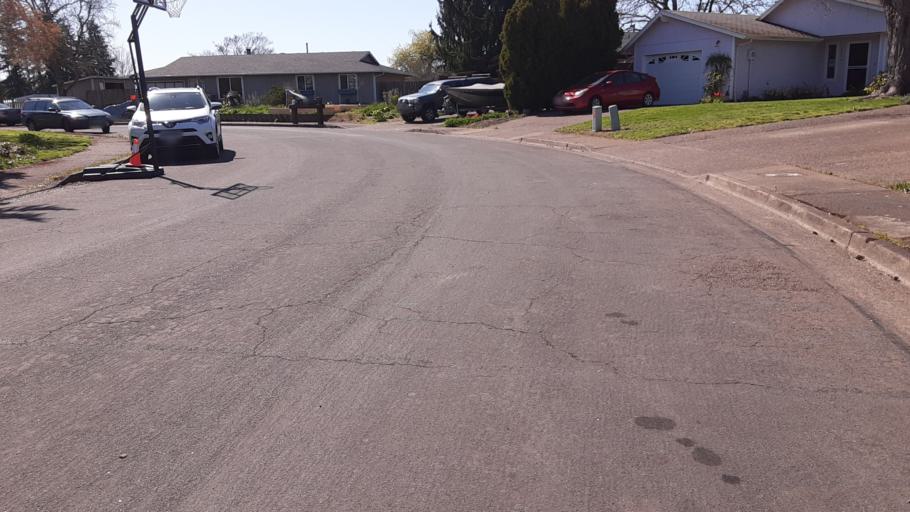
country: US
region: Oregon
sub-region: Benton County
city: Corvallis
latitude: 44.5408
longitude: -123.2627
